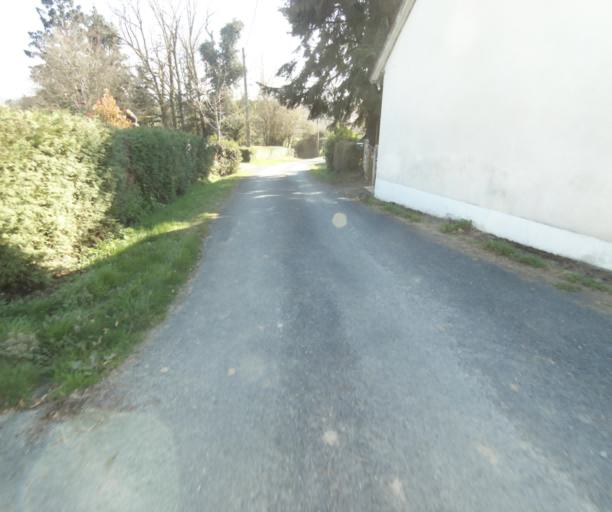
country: FR
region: Limousin
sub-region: Departement de la Correze
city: Saint-Mexant
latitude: 45.3275
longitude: 1.6236
